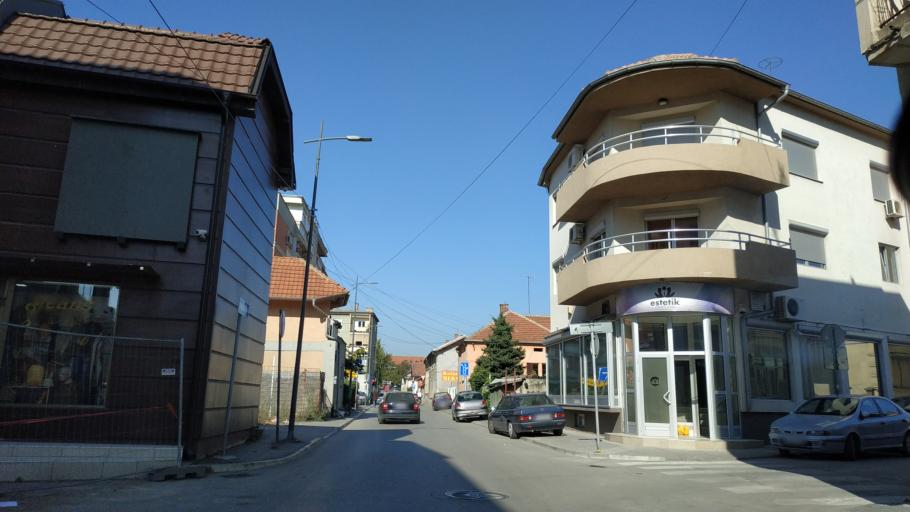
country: RS
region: Central Serbia
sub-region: Nisavski Okrug
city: Aleksinac
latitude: 43.5396
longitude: 21.7103
